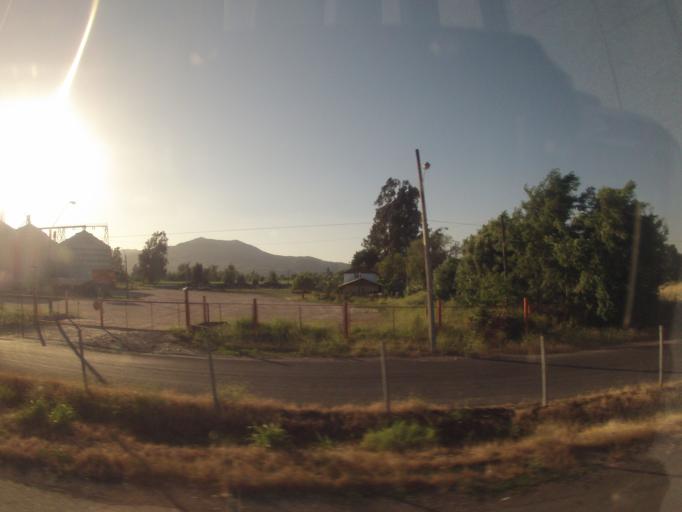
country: CL
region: O'Higgins
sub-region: Provincia de Colchagua
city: Chimbarongo
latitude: -34.6853
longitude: -71.0111
